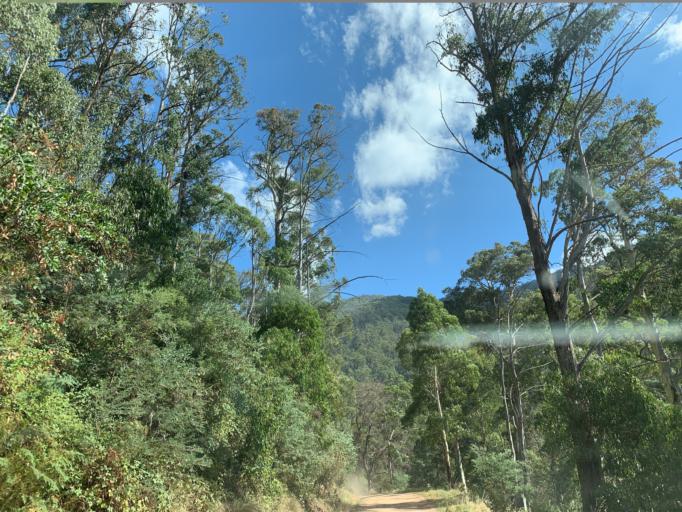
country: AU
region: Victoria
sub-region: Mansfield
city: Mansfield
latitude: -37.1027
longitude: 146.5028
